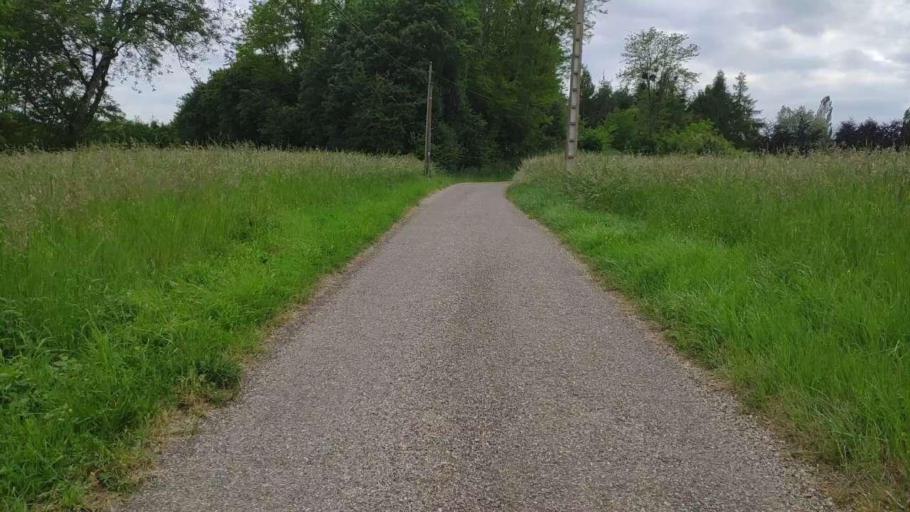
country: FR
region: Franche-Comte
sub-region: Departement du Jura
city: Bletterans
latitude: 46.7954
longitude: 5.5429
